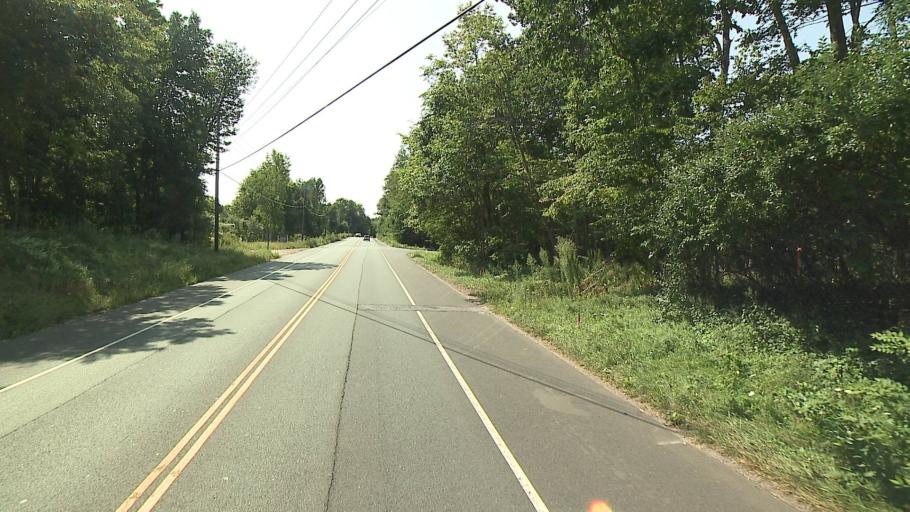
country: US
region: Connecticut
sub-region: Fairfield County
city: Newtown
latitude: 41.4225
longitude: -73.3555
